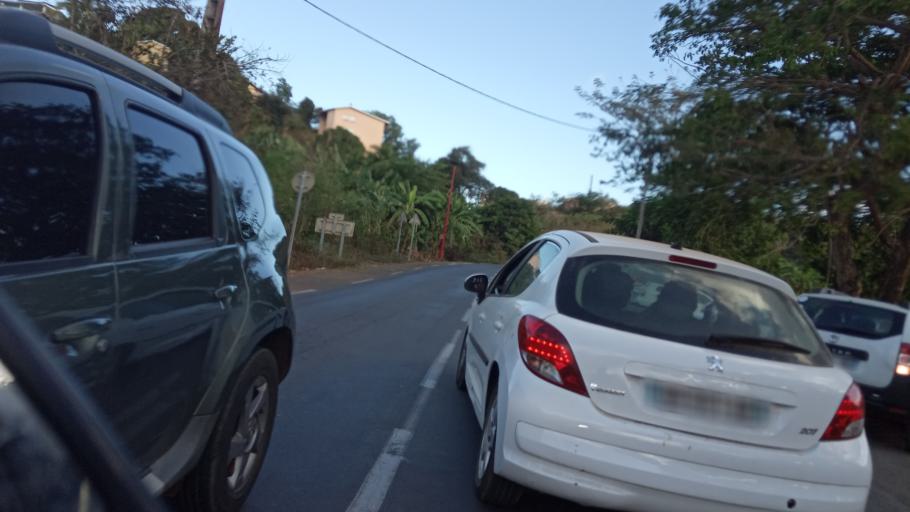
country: YT
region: Dembeni
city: Dembeni
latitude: -12.8467
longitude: 45.1910
